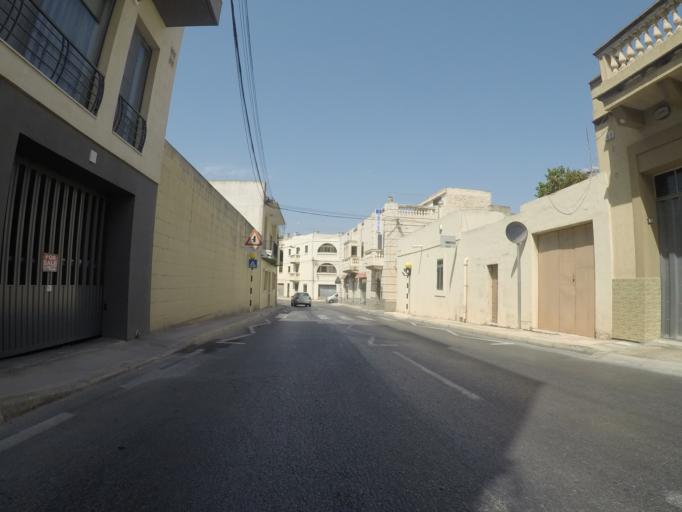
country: MT
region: Ir-Rabat
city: Rabat
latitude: 35.8758
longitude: 14.3973
